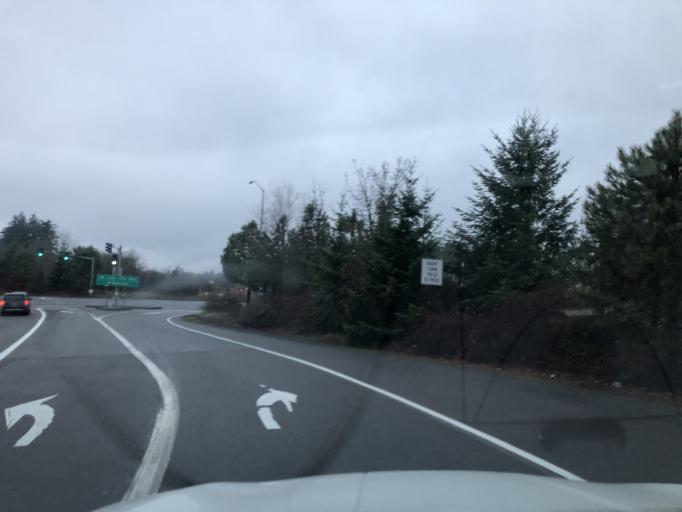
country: US
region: Oregon
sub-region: Washington County
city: Cedar Hills
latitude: 45.5147
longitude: -122.7922
